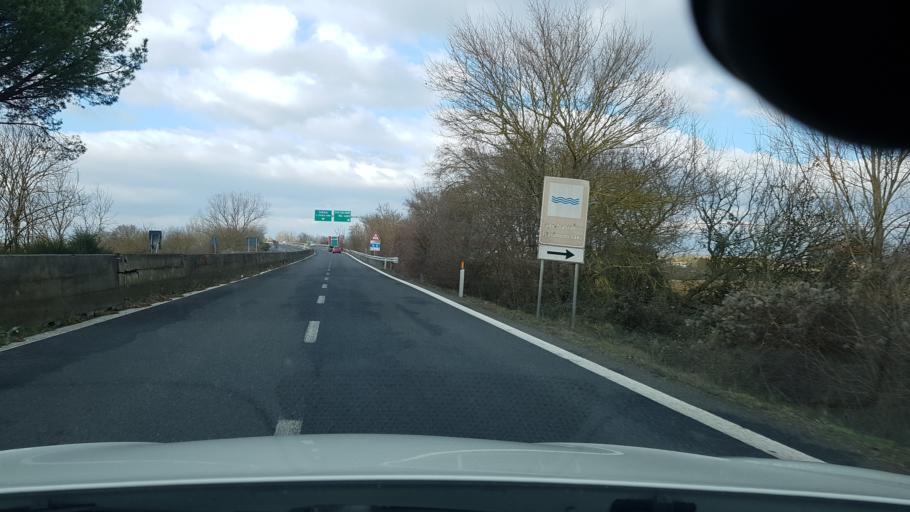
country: IT
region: Tuscany
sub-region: Province of Arezzo
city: Terontola
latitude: 43.1892
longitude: 12.0200
